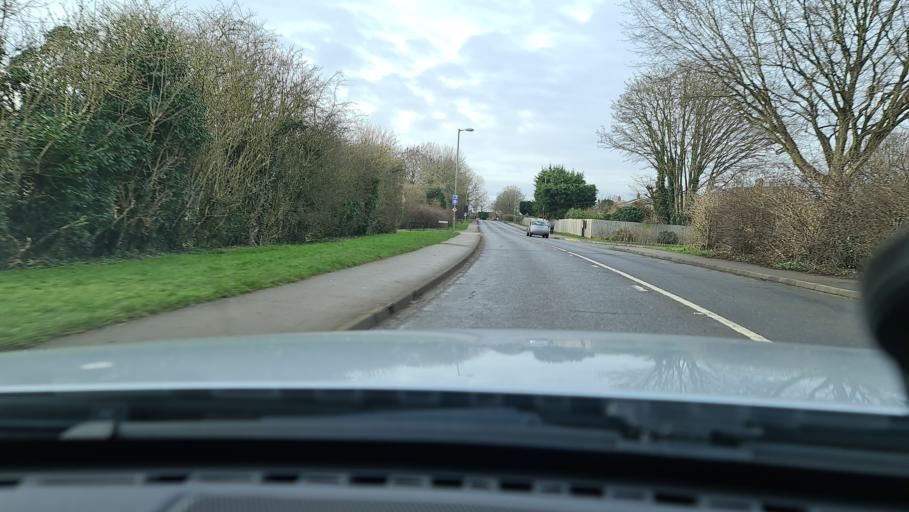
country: GB
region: England
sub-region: Oxfordshire
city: Adderbury
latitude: 52.0188
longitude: -1.3052
